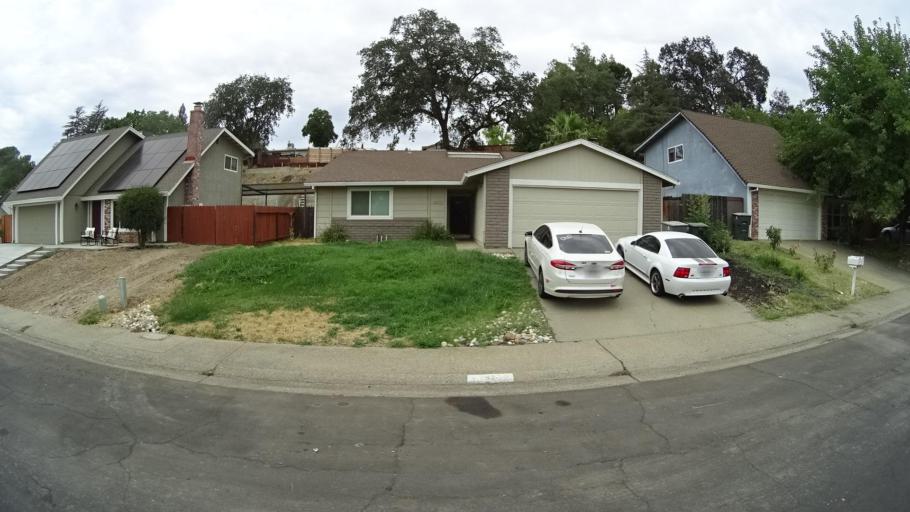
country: US
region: California
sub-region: Placer County
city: Rocklin
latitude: 38.7827
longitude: -121.2581
